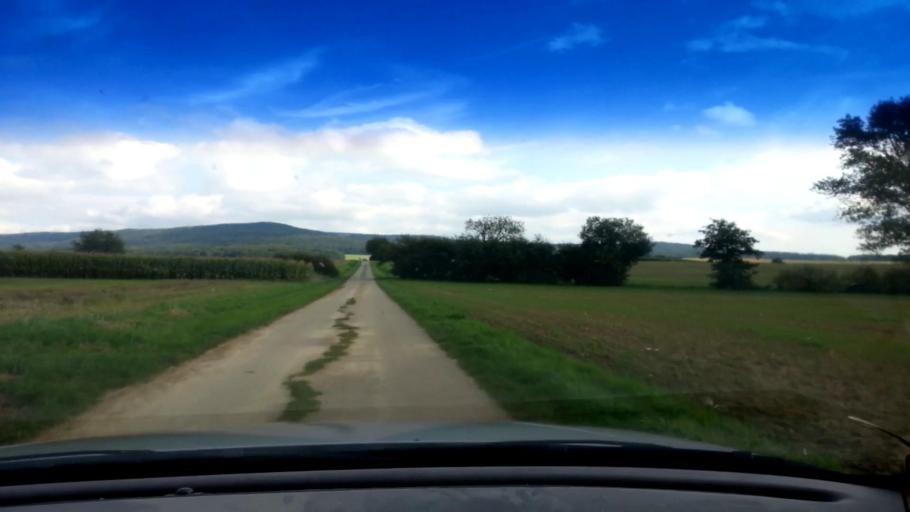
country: DE
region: Bavaria
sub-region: Upper Franconia
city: Schesslitz
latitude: 49.9546
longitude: 11.0032
